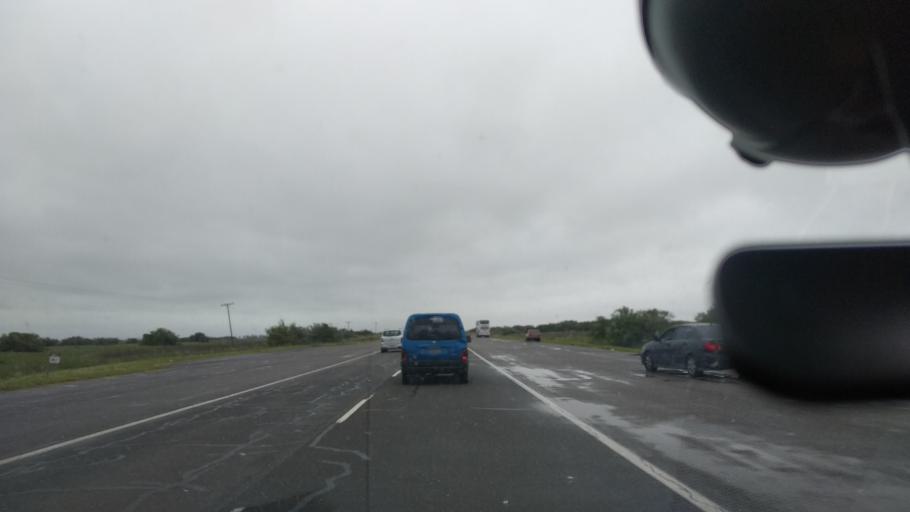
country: AR
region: Buenos Aires
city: Veronica
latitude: -35.7359
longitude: -57.3738
